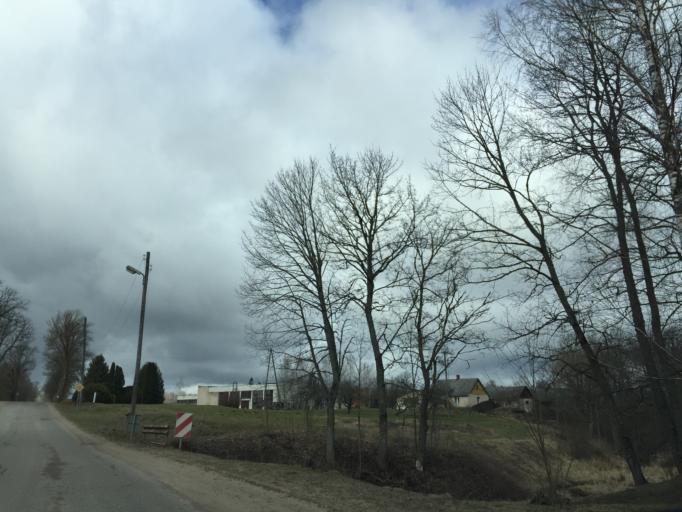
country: LV
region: Ilukste
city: Ilukste
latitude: 56.0699
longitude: 26.1266
